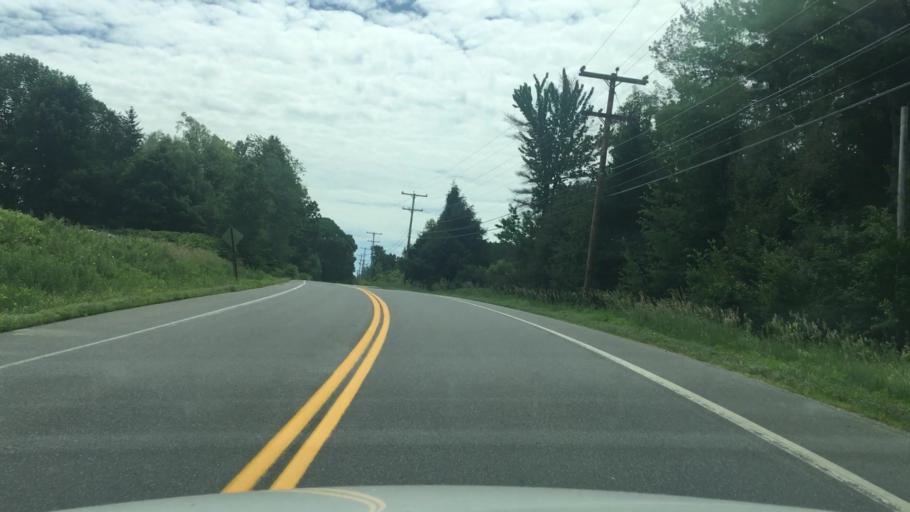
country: US
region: Maine
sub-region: Waldo County
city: Troy
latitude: 44.5679
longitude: -69.2787
